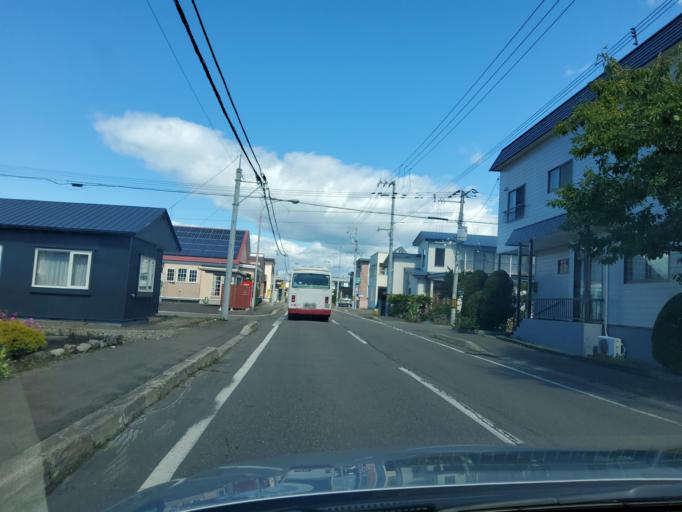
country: JP
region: Hokkaido
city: Otofuke
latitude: 42.9545
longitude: 143.2022
